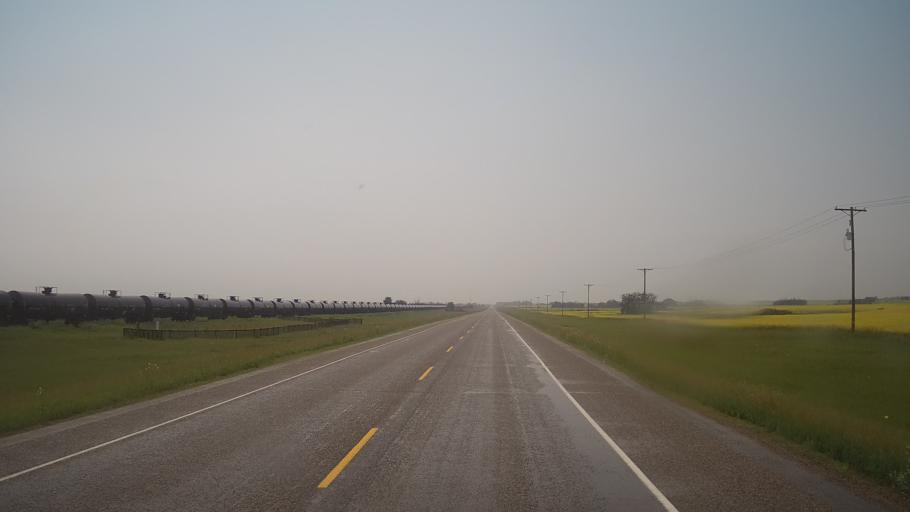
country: CA
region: Saskatchewan
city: Biggar
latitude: 52.1610
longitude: -108.2801
